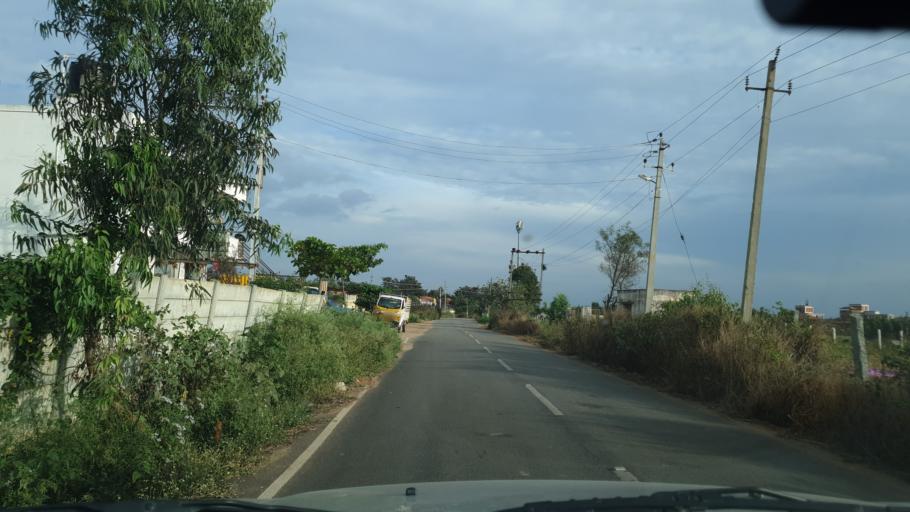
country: IN
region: Karnataka
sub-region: Bangalore Urban
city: Yelahanka
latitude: 13.1948
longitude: 77.6211
